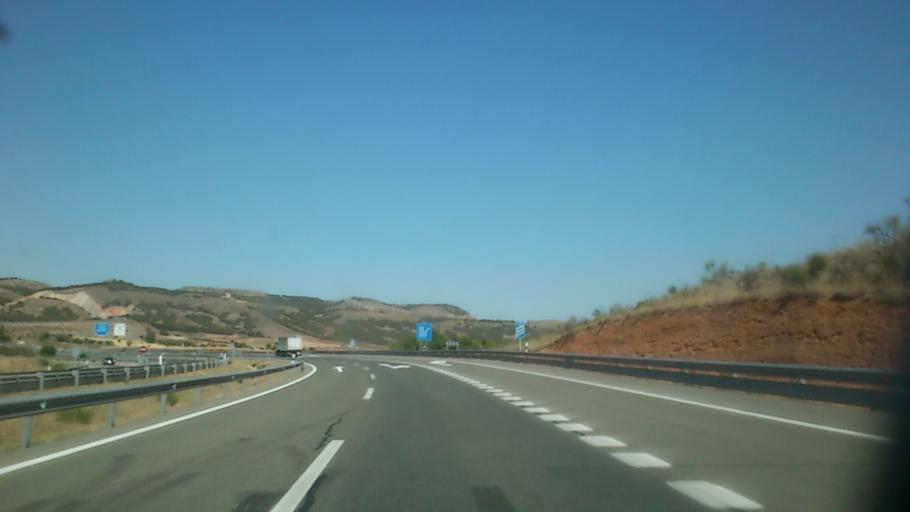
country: ES
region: Aragon
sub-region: Provincia de Zaragoza
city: Contamina
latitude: 41.3067
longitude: -1.9309
